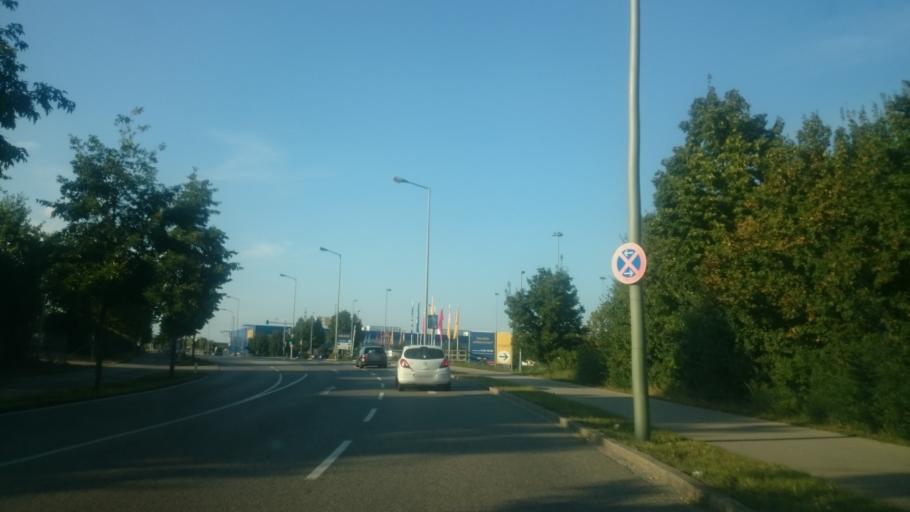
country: DE
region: Bavaria
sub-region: Swabia
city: Gersthofen
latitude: 48.4019
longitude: 10.8703
